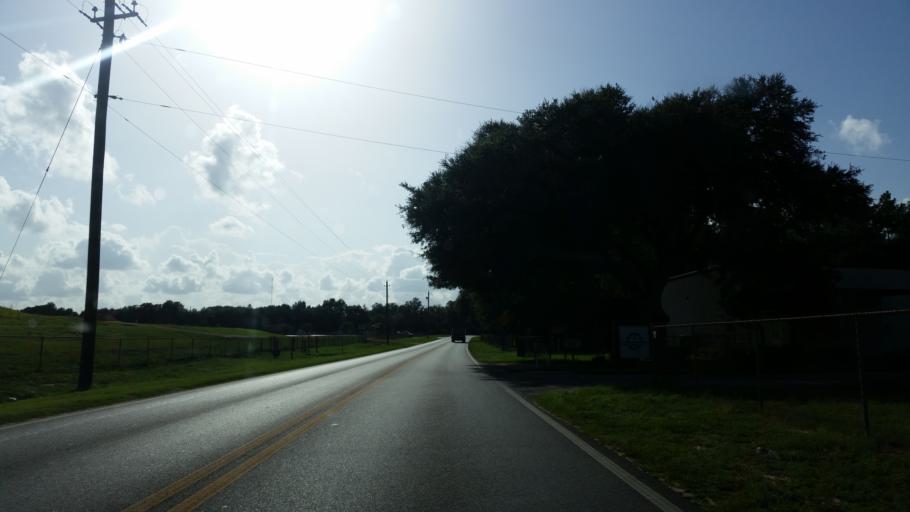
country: US
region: Florida
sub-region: Santa Rosa County
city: Bagdad
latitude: 30.5829
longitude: -87.0576
